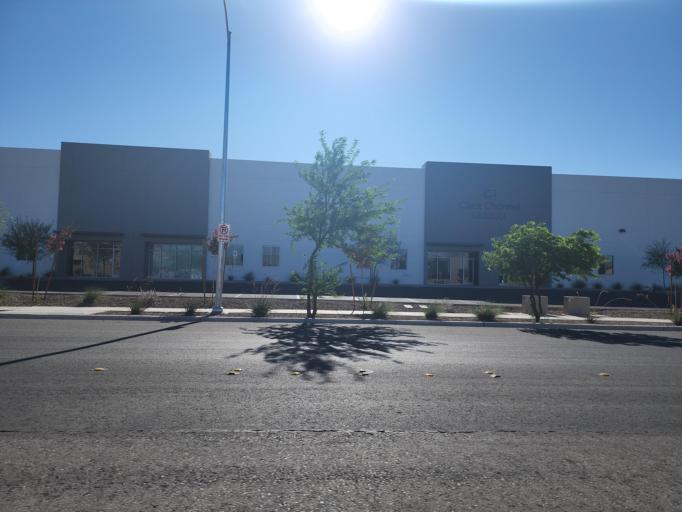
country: US
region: Nevada
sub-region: Clark County
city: Spring Valley
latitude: 36.0733
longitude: -115.2701
